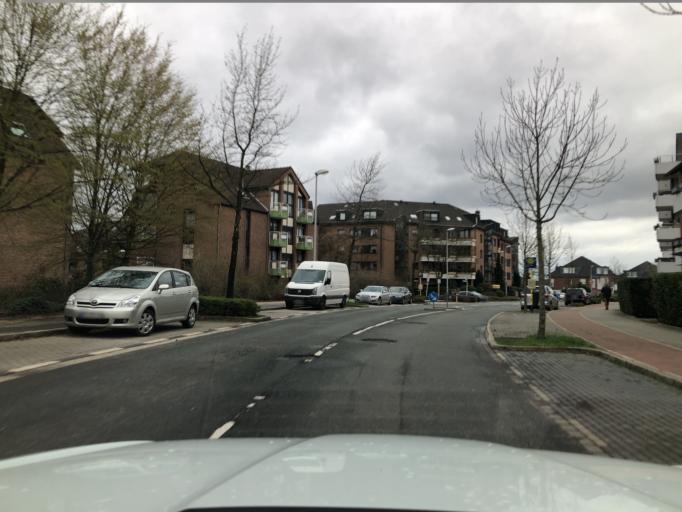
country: DE
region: North Rhine-Westphalia
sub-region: Regierungsbezirk Dusseldorf
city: Muelheim (Ruhr)
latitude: 51.3958
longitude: 6.8647
